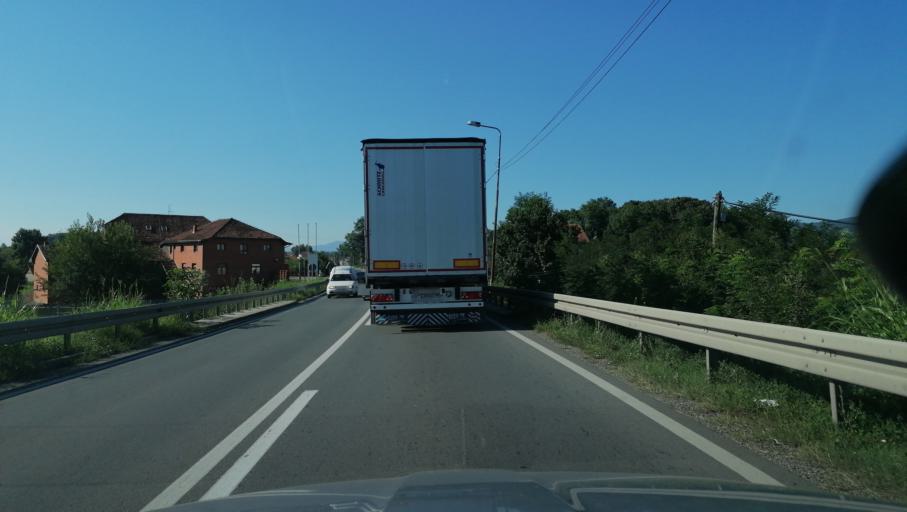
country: RS
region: Central Serbia
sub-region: Raski Okrug
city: Kraljevo
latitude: 43.7475
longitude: 20.6636
